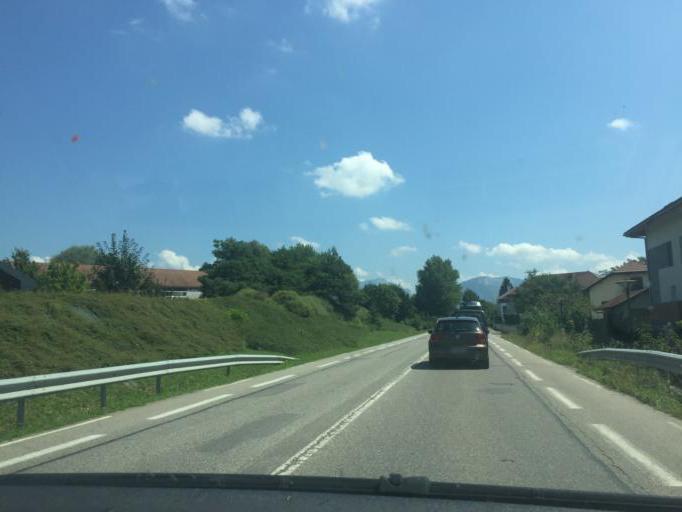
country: FR
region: Rhone-Alpes
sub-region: Departement de la Haute-Savoie
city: Poisy
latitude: 45.9201
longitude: 6.0608
